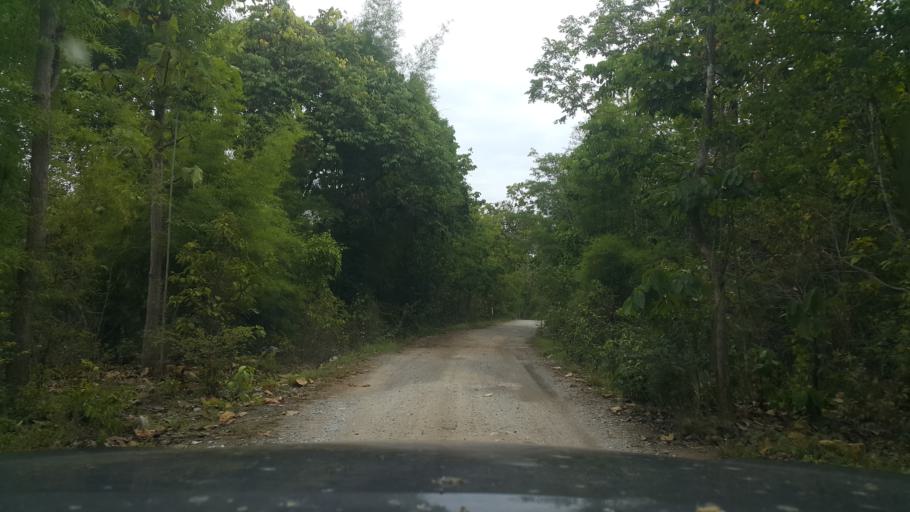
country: TH
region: Chiang Mai
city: San Pa Tong
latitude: 18.6497
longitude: 98.8500
